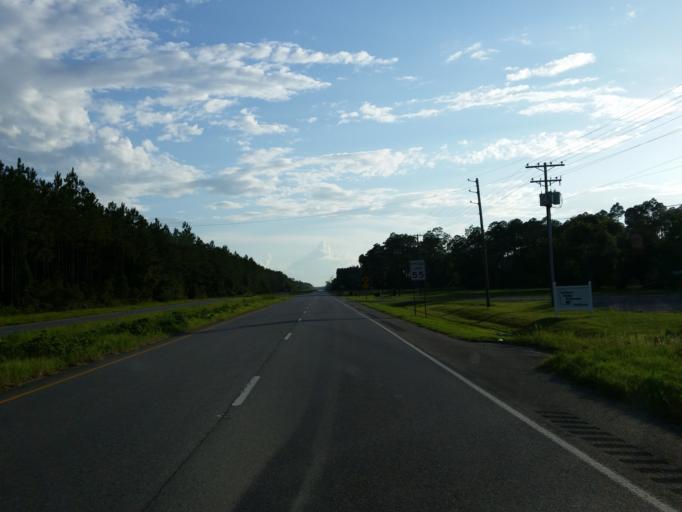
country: US
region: Georgia
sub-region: Clinch County
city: Homerville
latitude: 31.0293
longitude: -82.7817
